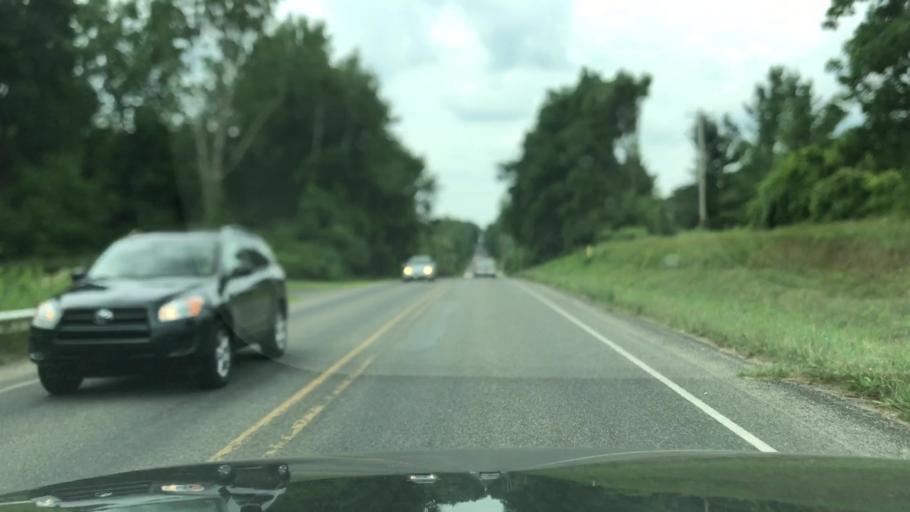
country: US
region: Michigan
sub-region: Kent County
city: East Grand Rapids
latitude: 42.9687
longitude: -85.5610
